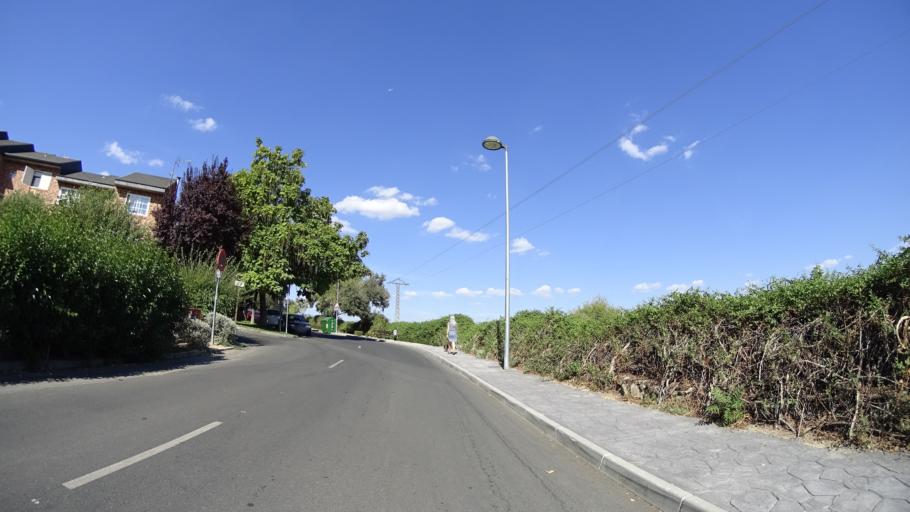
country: ES
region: Madrid
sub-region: Provincia de Madrid
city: Navalquejigo
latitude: 40.6079
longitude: -4.0252
